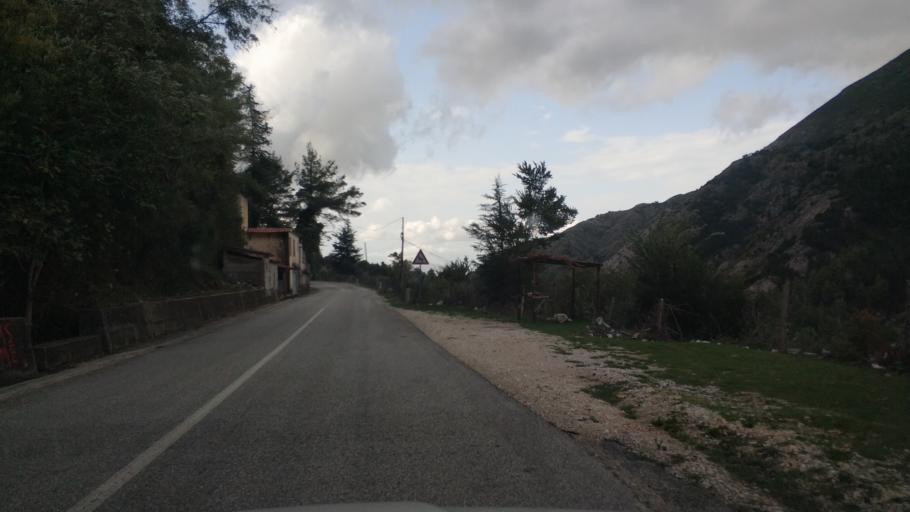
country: AL
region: Vlore
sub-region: Rrethi i Vlores
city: Orikum
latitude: 40.2459
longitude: 19.5493
